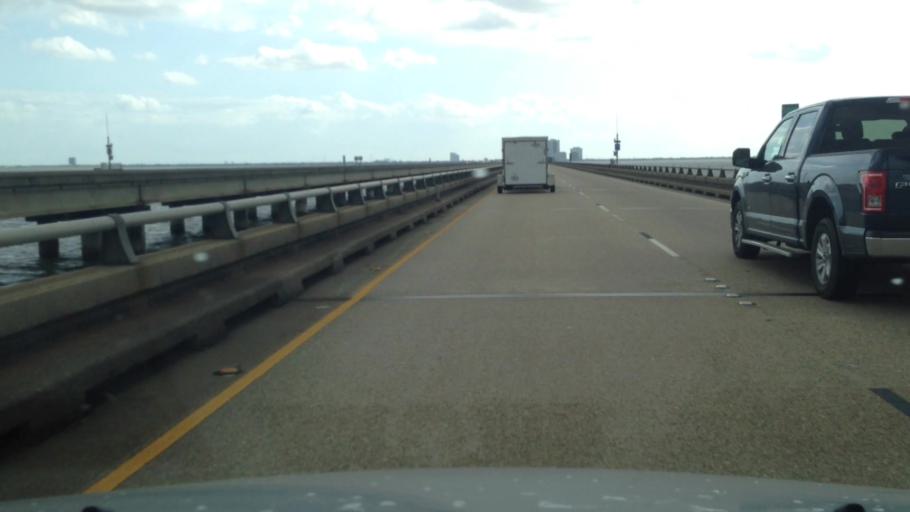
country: US
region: Louisiana
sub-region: Jefferson Parish
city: Metairie
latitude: 30.0650
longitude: -90.1465
